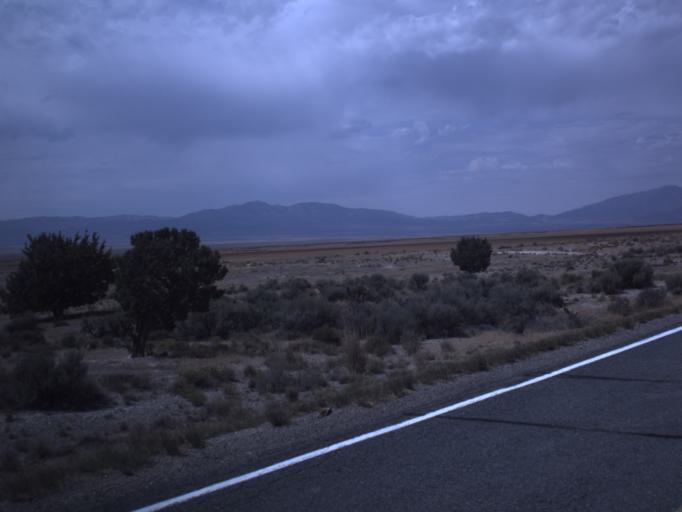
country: US
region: Utah
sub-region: Utah County
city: Eagle Mountain
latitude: 40.2385
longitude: -112.2021
